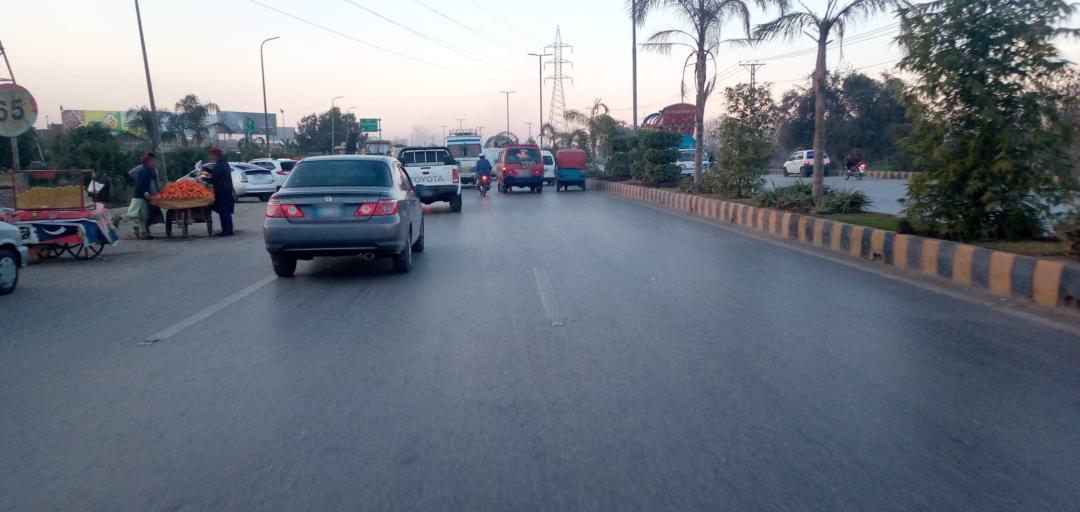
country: PK
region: Khyber Pakhtunkhwa
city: Peshawar
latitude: 34.0254
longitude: 71.6193
